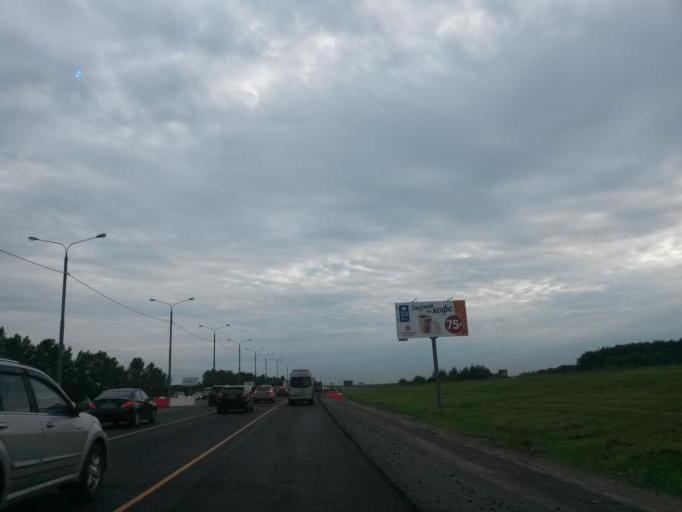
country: RU
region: Moskovskaya
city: Klimovsk
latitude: 55.3428
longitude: 37.5845
